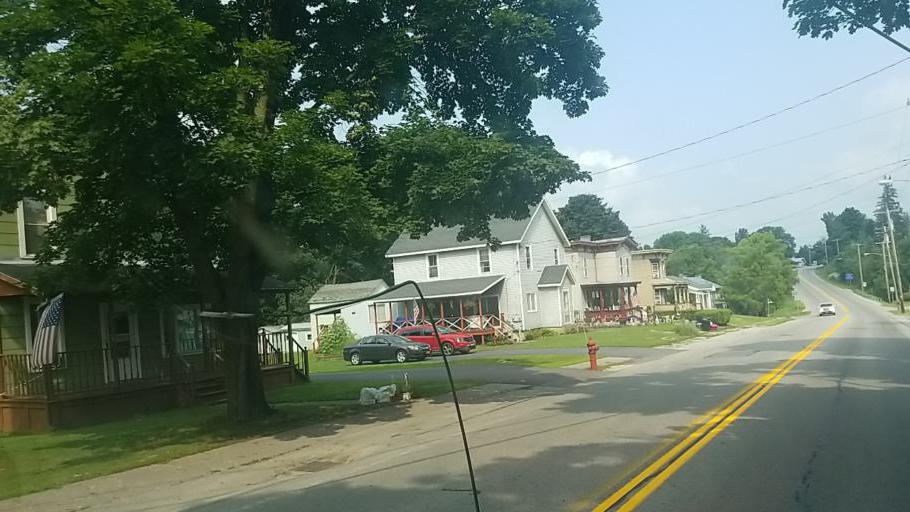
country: US
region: New York
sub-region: Montgomery County
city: Fort Plain
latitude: 42.9361
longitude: -74.6146
